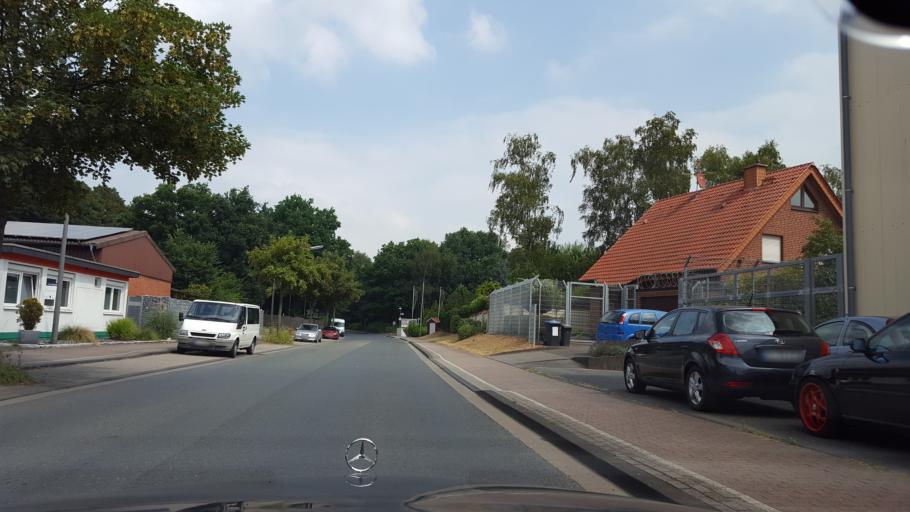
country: DE
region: North Rhine-Westphalia
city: Marl
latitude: 51.6729
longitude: 7.1544
